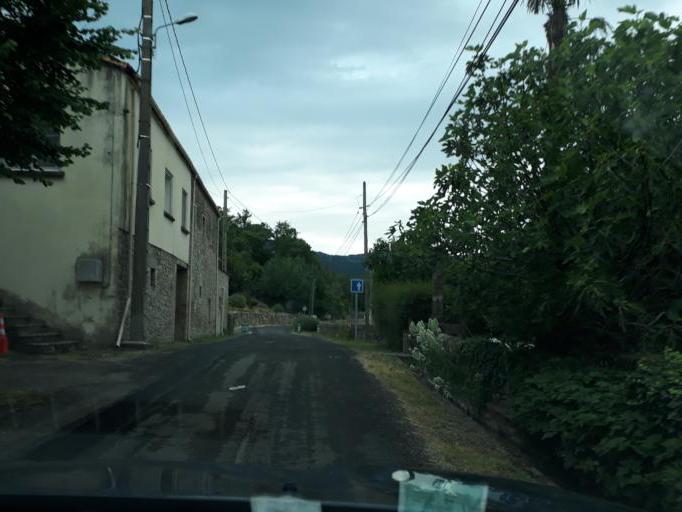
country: FR
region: Languedoc-Roussillon
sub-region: Departement de l'Herault
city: Lodeve
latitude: 43.7676
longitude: 3.3044
